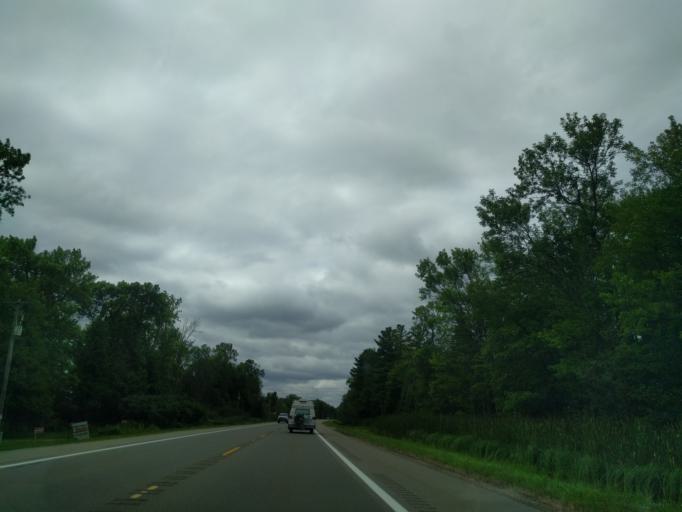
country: US
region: Michigan
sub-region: Menominee County
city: Menominee
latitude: 45.2182
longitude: -87.5188
